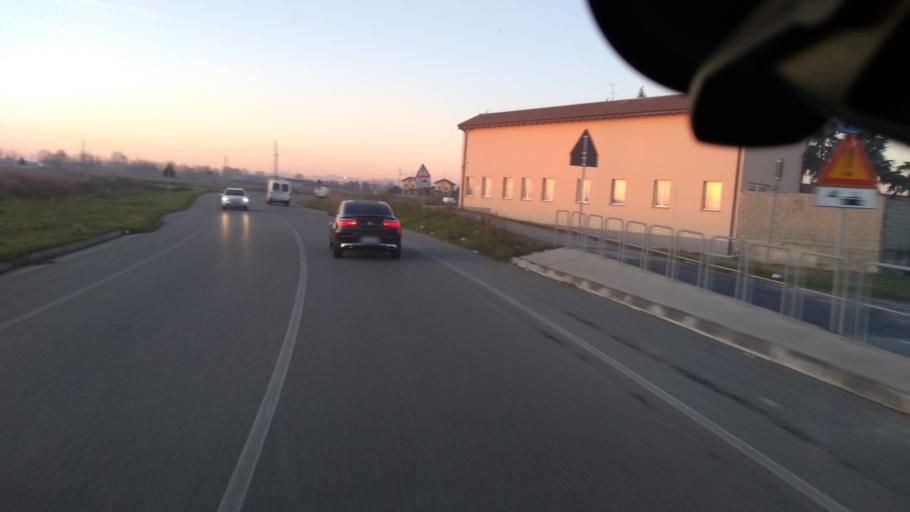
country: IT
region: Lombardy
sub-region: Provincia di Bergamo
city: Calvenzano
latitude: 45.5049
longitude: 9.5964
